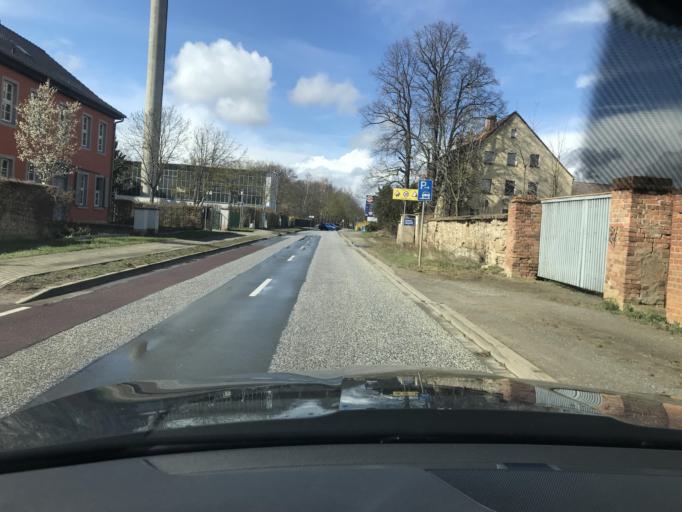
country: DE
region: Saxony-Anhalt
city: Hoym
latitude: 51.7836
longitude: 11.3214
